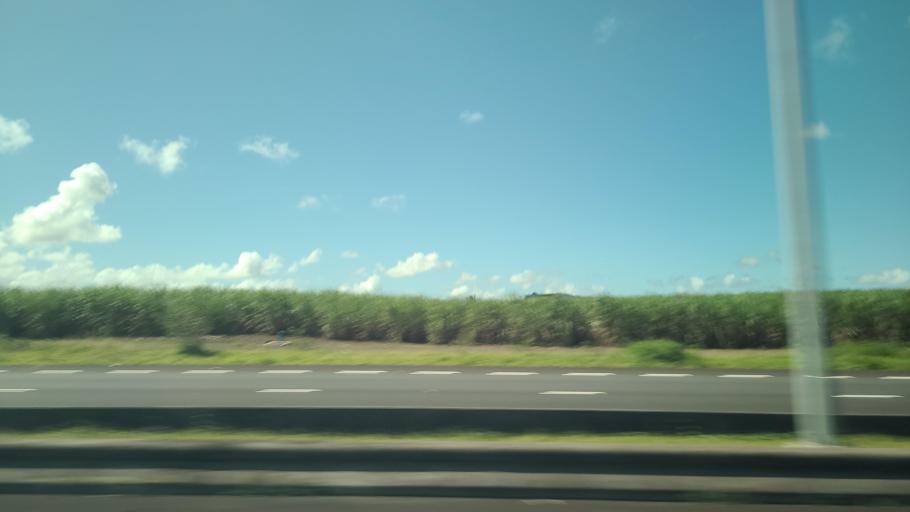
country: MU
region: Grand Port
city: Plaine Magnien
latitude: -20.4388
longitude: 57.6621
